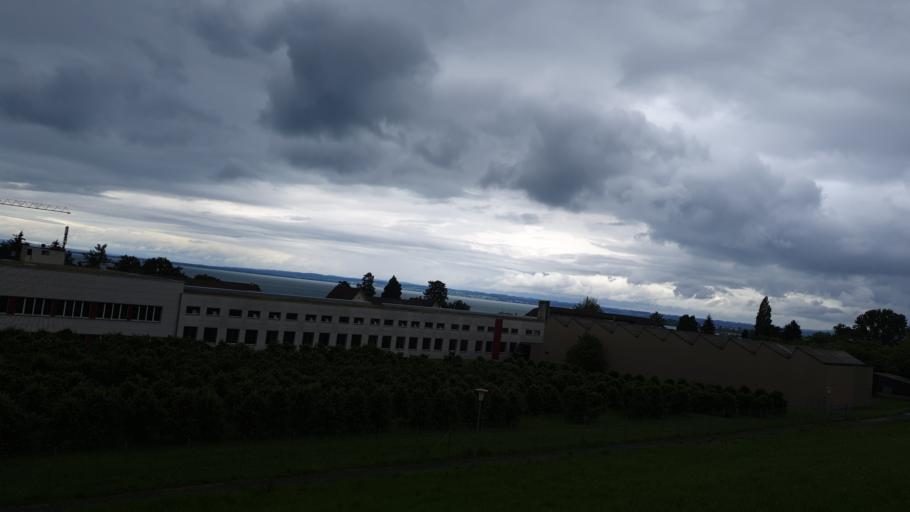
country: CH
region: Saint Gallen
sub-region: Wahlkreis Rorschach
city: Rorschach
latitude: 47.4767
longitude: 9.5185
